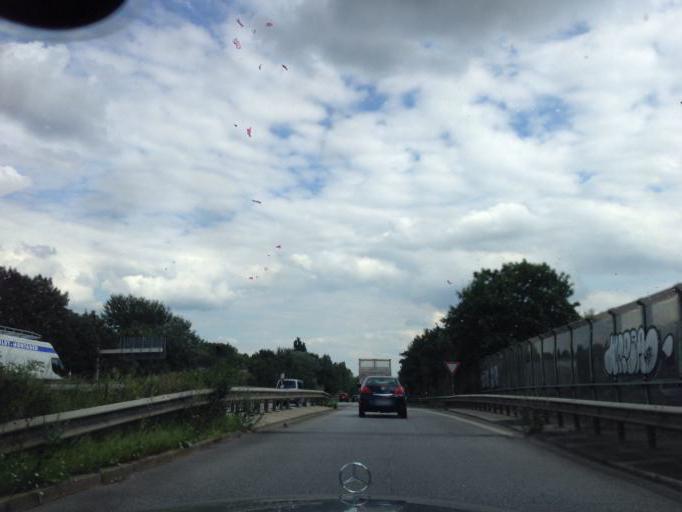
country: DE
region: Hamburg
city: Marienthal
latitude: 53.5441
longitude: 10.0852
